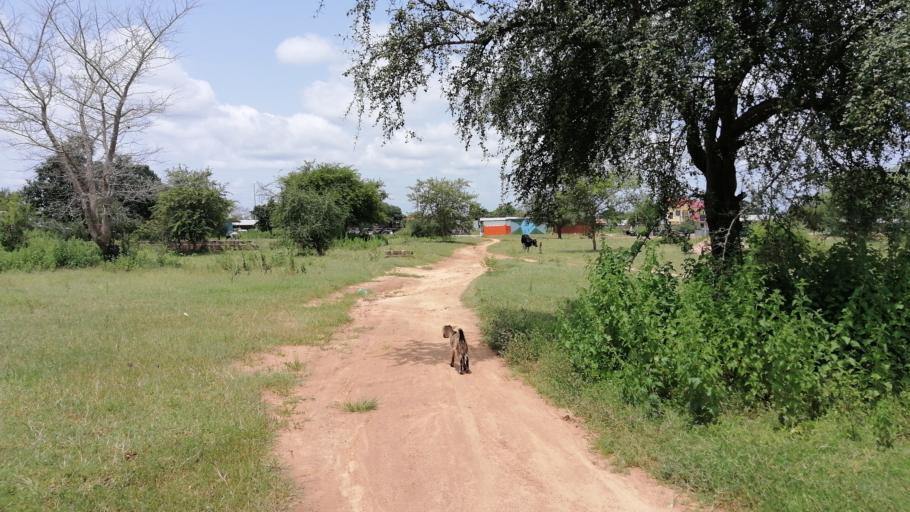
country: GH
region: Upper East
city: Bolgatanga
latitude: 10.8063
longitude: -0.8921
